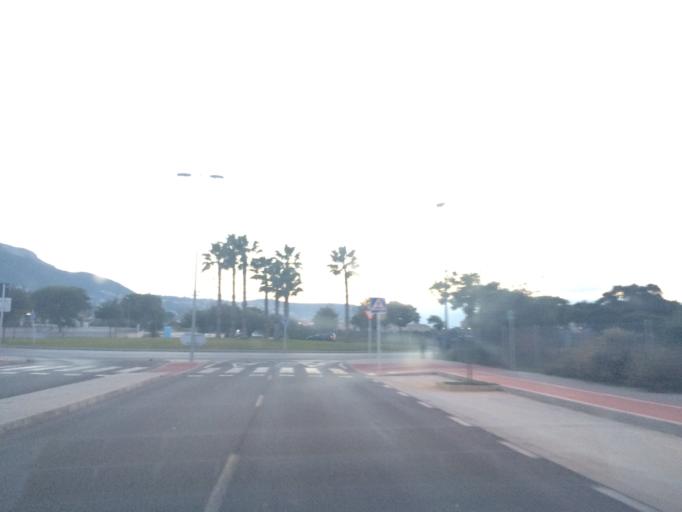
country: ES
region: Valencia
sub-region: Provincia de Alicante
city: Denia
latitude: 38.8338
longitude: 0.1118
